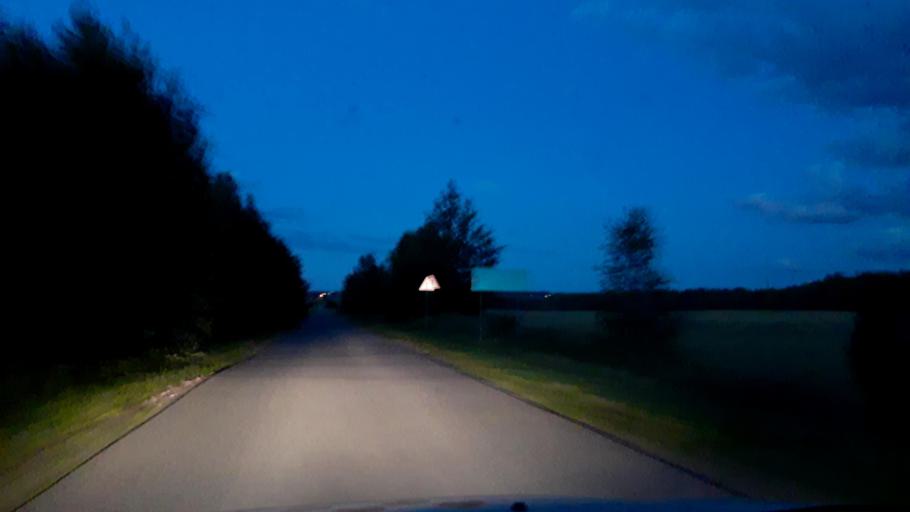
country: RU
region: Nizjnij Novgorod
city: Pamyat' Parizhskoy Kommuny
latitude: 56.0589
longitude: 44.4840
